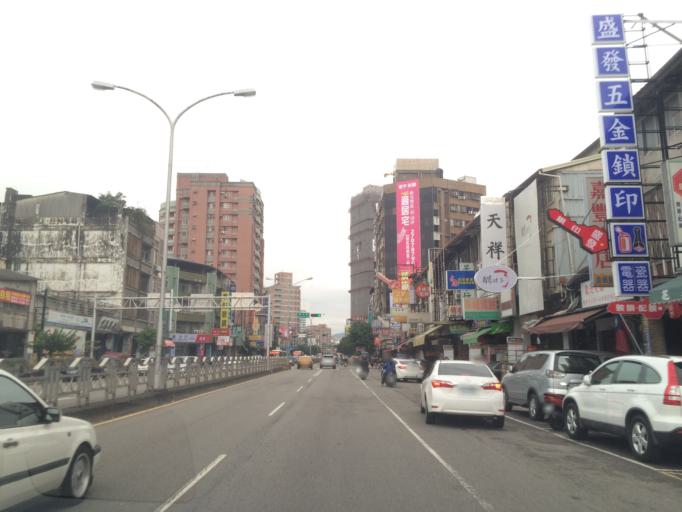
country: TW
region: Taiwan
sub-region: Taichung City
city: Taichung
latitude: 24.1551
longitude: 120.6867
